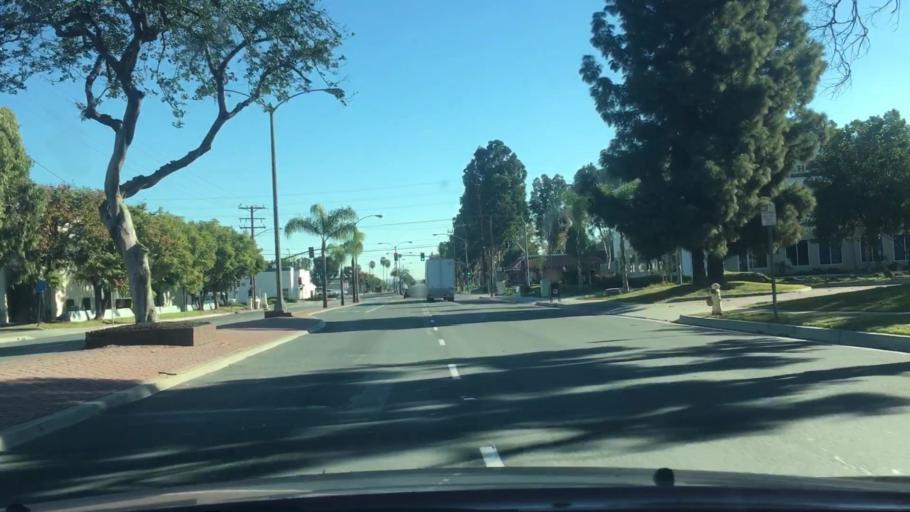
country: US
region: California
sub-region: Los Angeles County
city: Cerritos
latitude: 33.8878
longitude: -118.0480
